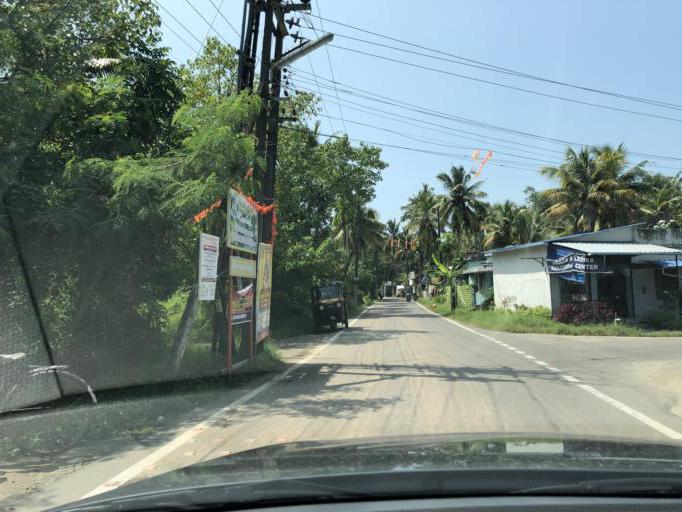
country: IN
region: Kerala
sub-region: Ernakulam
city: Cochin
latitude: 9.9896
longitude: 76.2288
